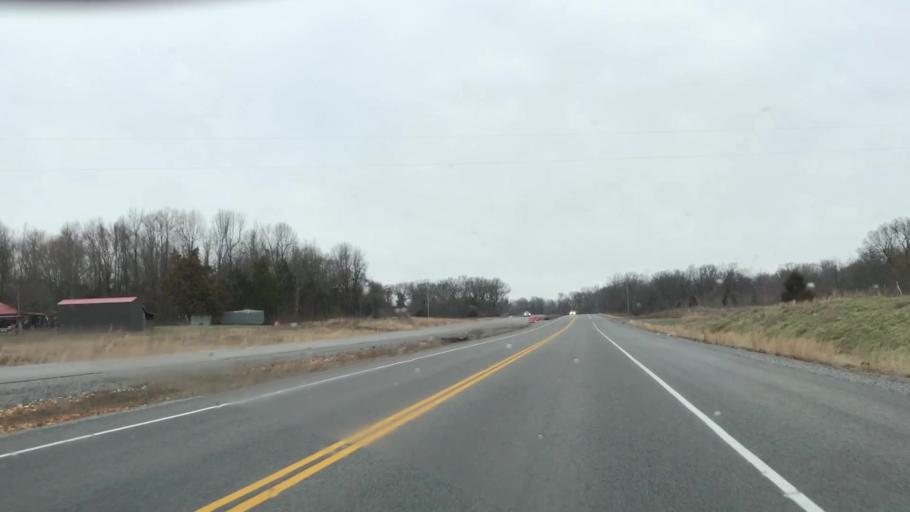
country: US
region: Kentucky
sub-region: Trigg County
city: Cadiz
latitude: 36.8289
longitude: -87.8678
